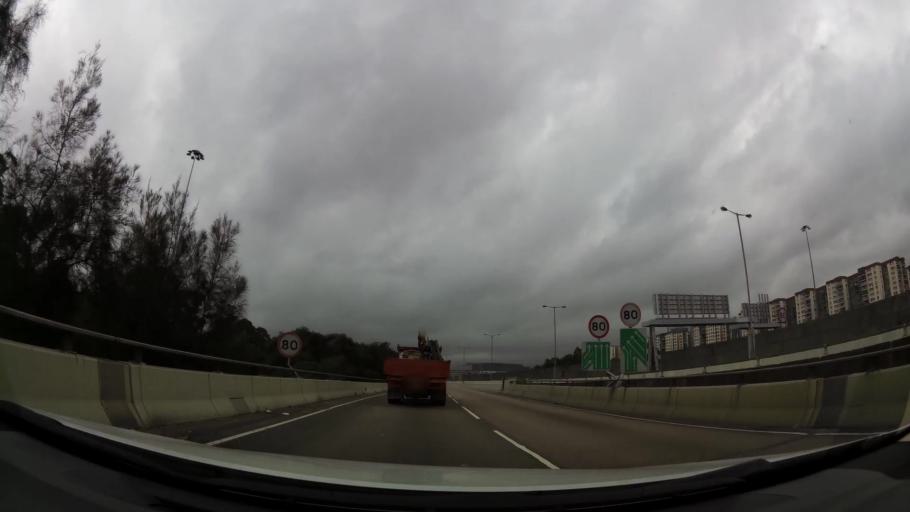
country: HK
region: Sham Shui Po
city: Sham Shui Po
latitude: 22.3322
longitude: 114.1404
